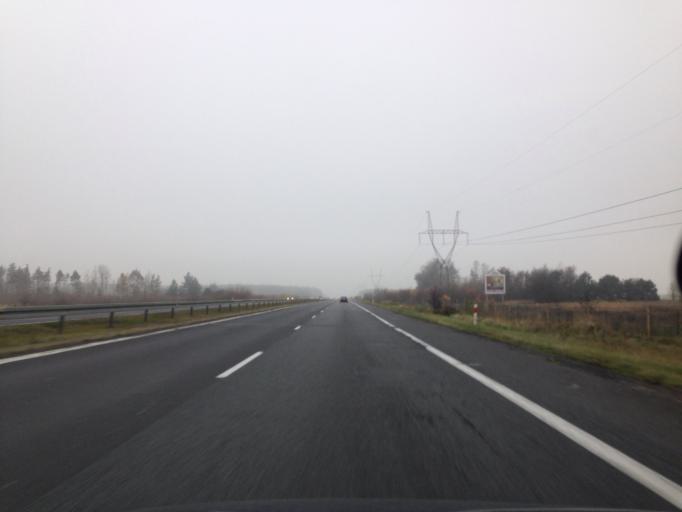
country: PL
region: Lodz Voivodeship
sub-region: Powiat radomszczanski
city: Radomsko
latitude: 51.1243
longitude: 19.4070
